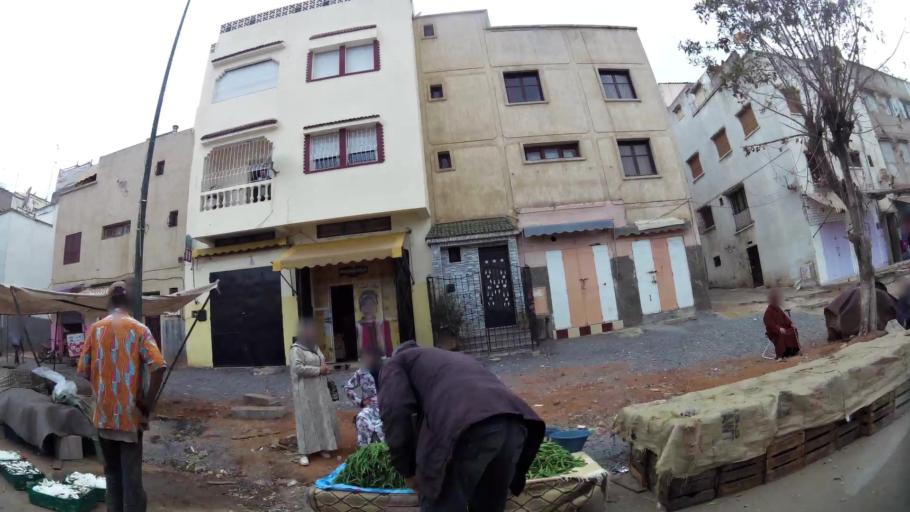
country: MA
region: Rabat-Sale-Zemmour-Zaer
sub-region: Rabat
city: Rabat
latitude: 33.9953
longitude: -6.8139
